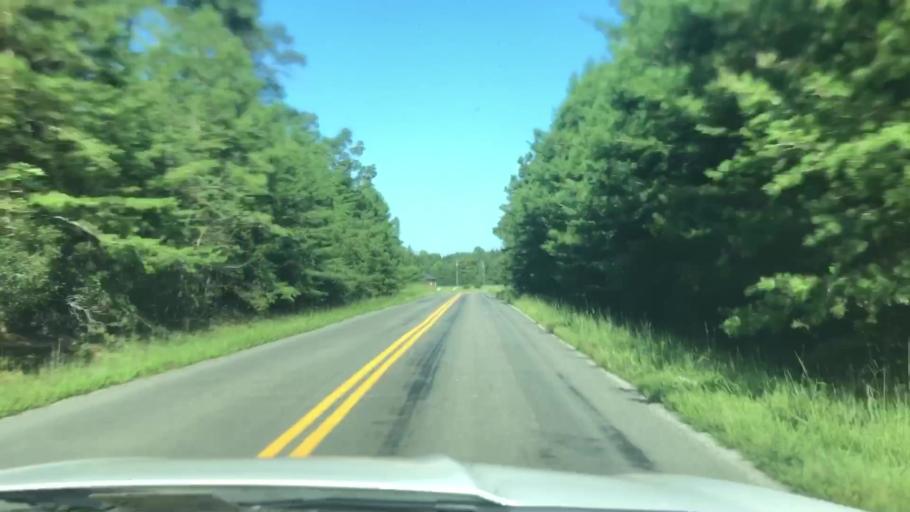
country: US
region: Virginia
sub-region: New Kent County
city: New Kent
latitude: 37.4850
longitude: -76.9300
